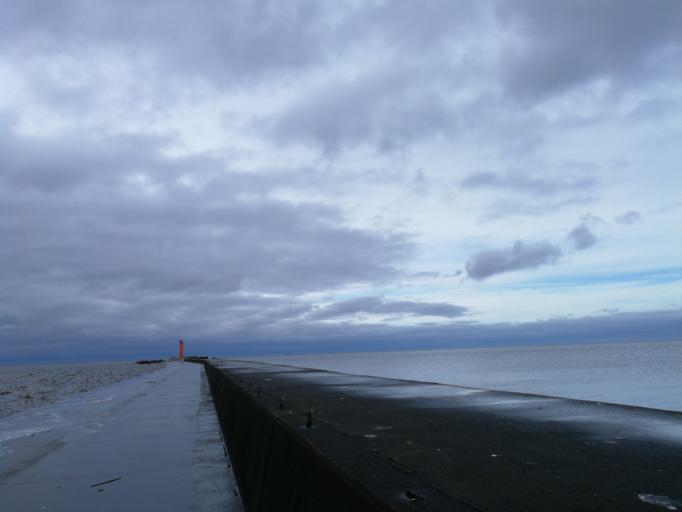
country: LV
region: Riga
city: Daugavgriva
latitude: 57.0675
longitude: 24.0192
